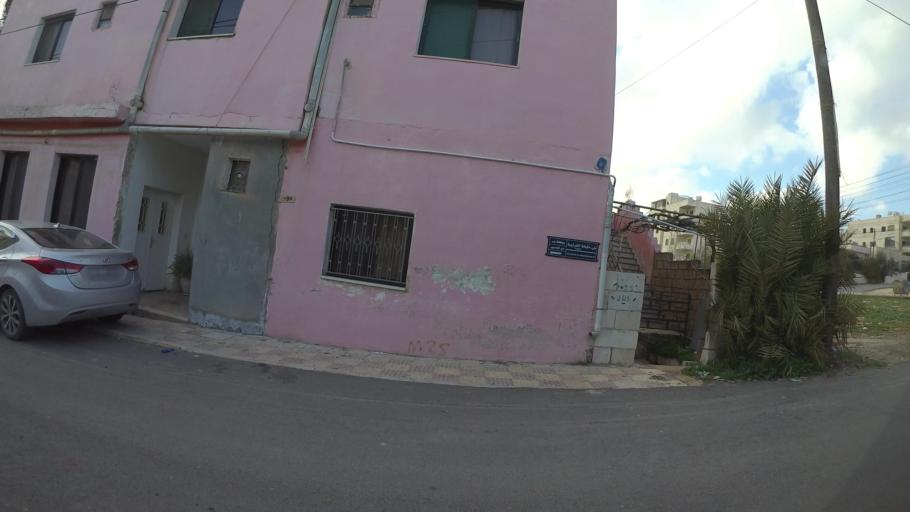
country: JO
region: Amman
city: Al Bunayyat ash Shamaliyah
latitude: 31.9086
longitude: 35.8852
